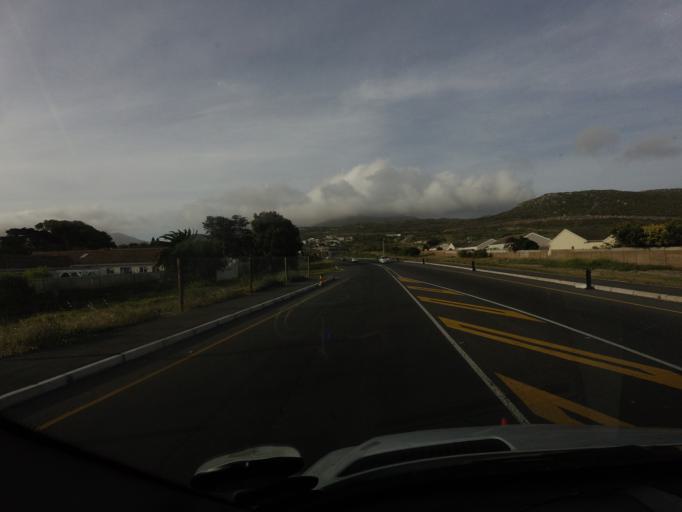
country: ZA
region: Western Cape
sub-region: City of Cape Town
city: Constantia
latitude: -34.1184
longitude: 18.3921
